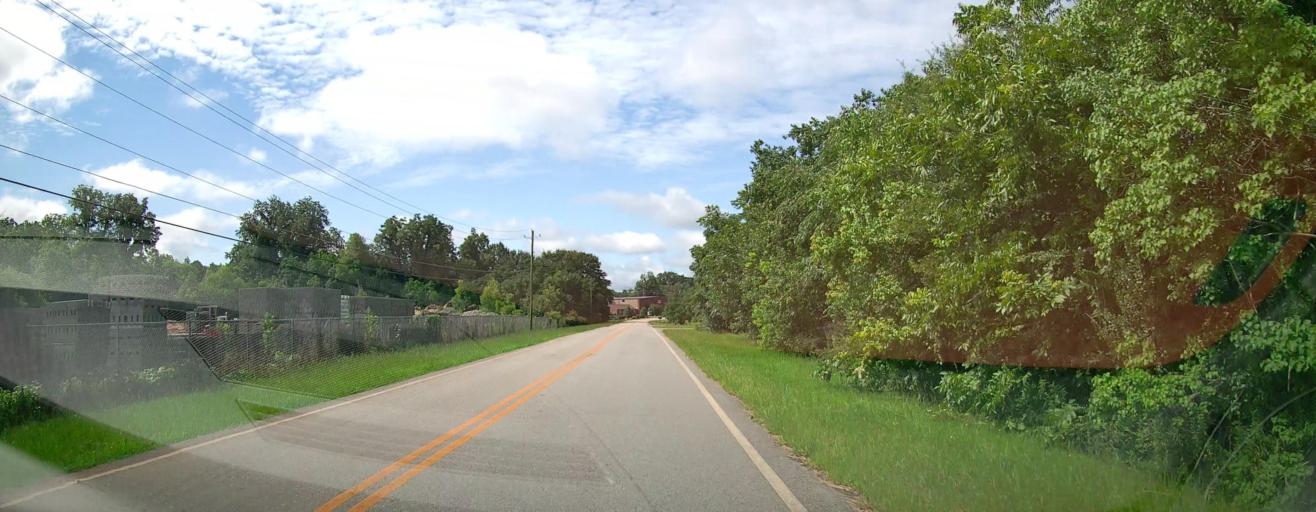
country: US
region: Georgia
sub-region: Peach County
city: Byron
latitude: 32.6506
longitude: -83.7364
